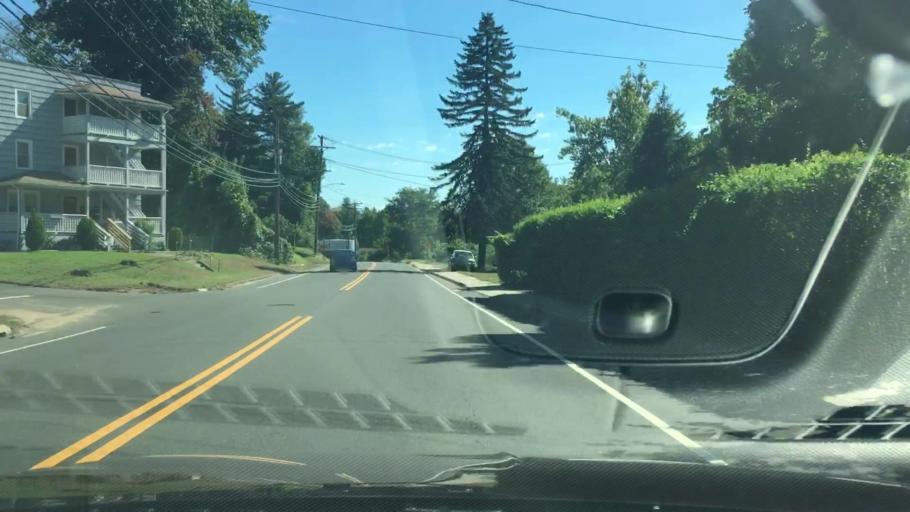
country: US
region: Connecticut
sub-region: Hartford County
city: Bristol
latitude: 41.6810
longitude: -72.9063
